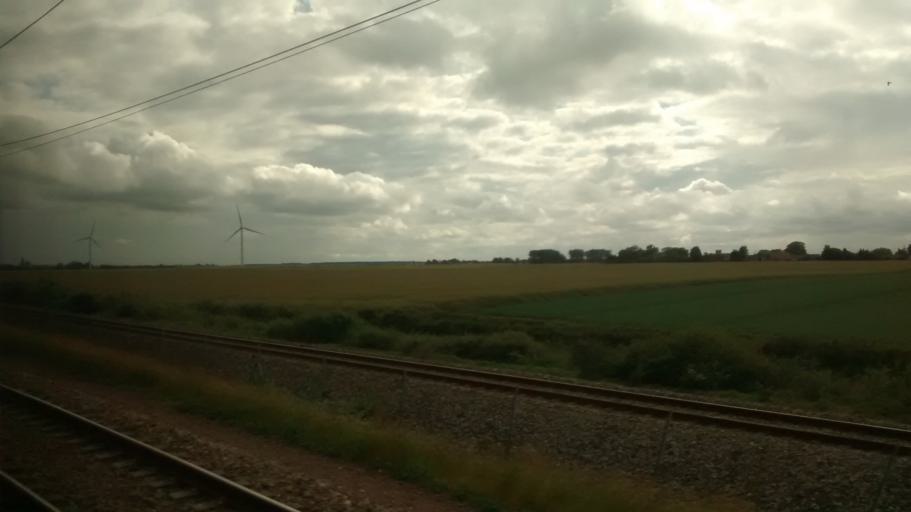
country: FR
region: Centre
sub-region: Departement d'Eure-et-Loir
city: Voves
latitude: 48.3092
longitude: 1.6593
